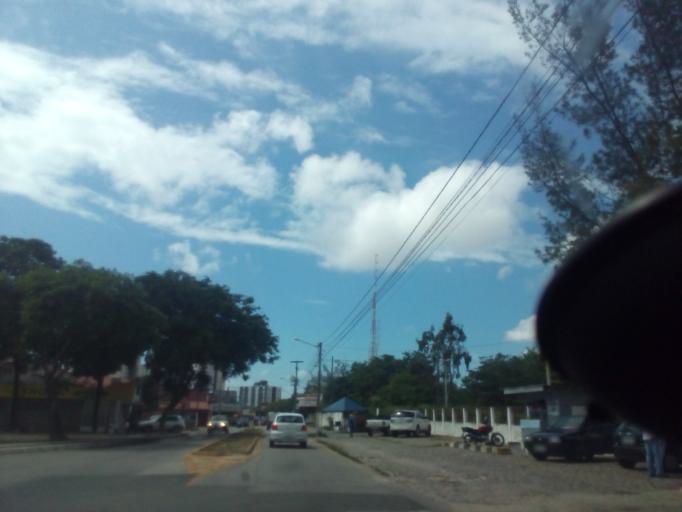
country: BR
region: Rio Grande do Norte
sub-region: Natal
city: Natal
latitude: -5.8383
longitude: -35.2177
